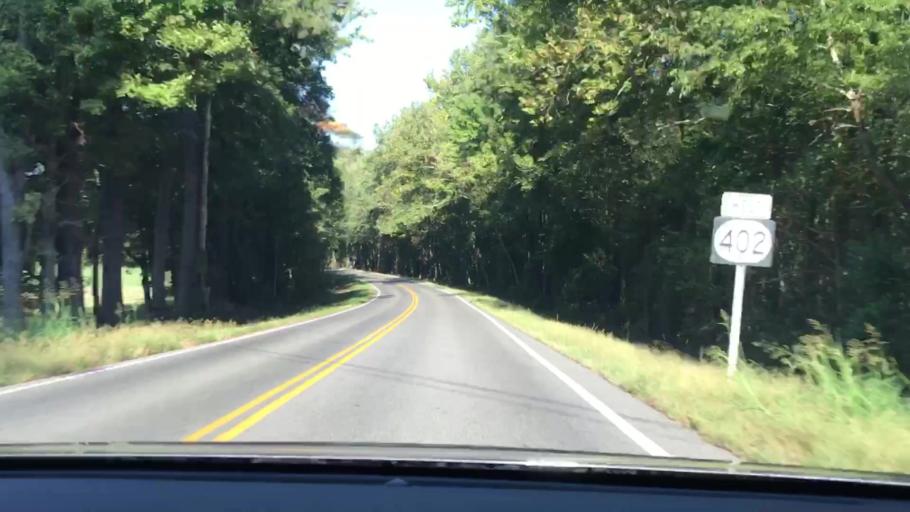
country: US
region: Kentucky
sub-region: Marshall County
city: Benton
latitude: 36.7677
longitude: -88.2744
